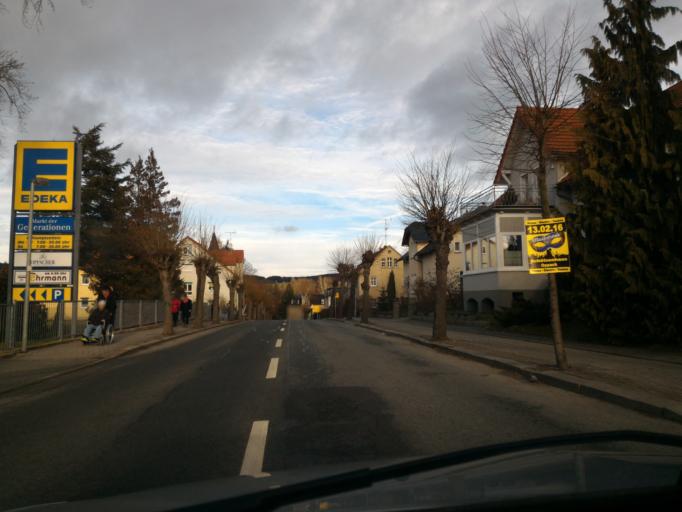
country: DE
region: Saxony
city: Oppach
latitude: 51.0566
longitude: 14.5045
